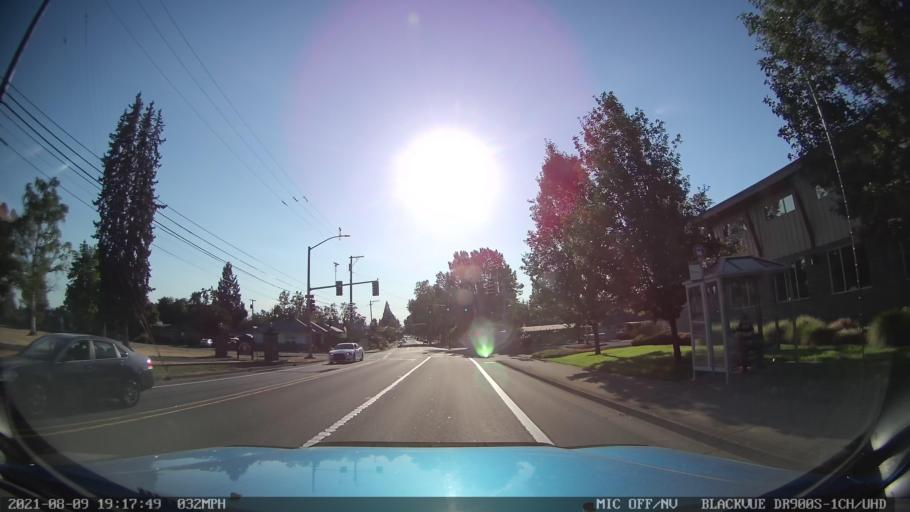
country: US
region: Oregon
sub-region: Marion County
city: Four Corners
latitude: 44.9400
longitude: -123.0079
